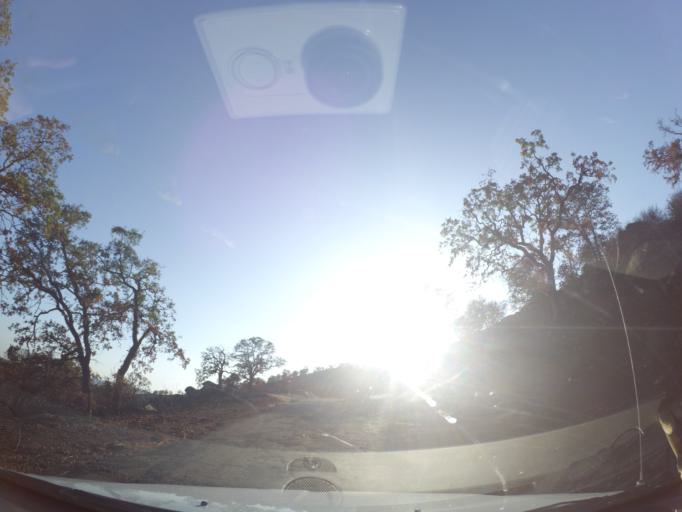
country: US
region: California
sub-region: Mariposa County
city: Mariposa
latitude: 37.5062
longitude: -120.1012
